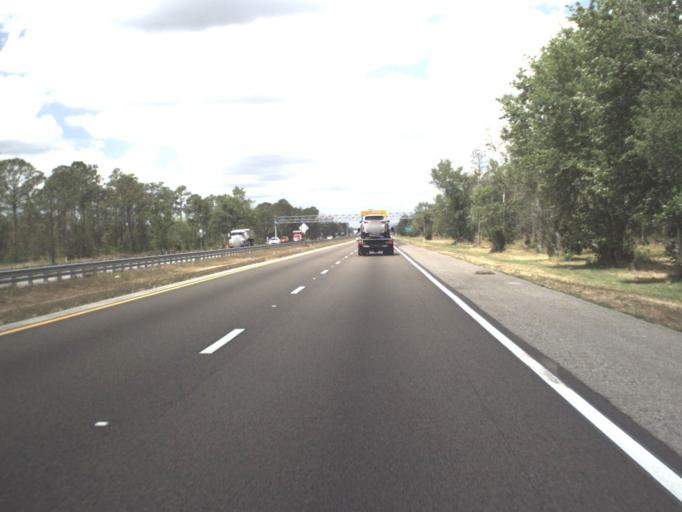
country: US
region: Florida
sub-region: Orange County
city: Alafaya
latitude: 28.4517
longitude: -81.1890
